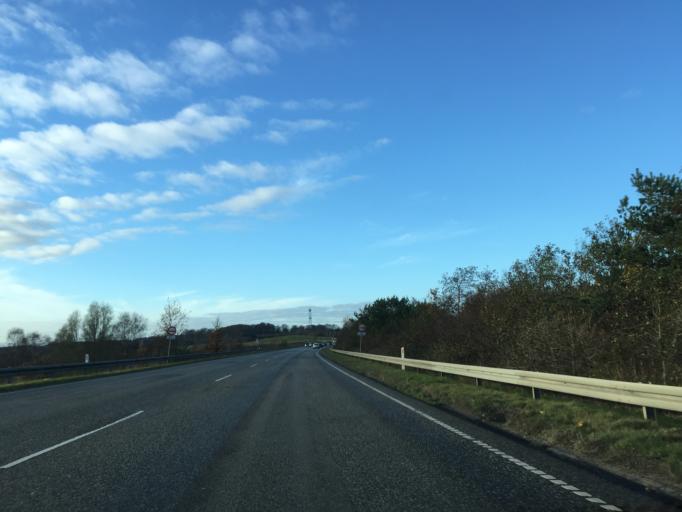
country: DK
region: Central Jutland
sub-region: Favrskov Kommune
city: Soften
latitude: 56.1881
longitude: 10.0817
